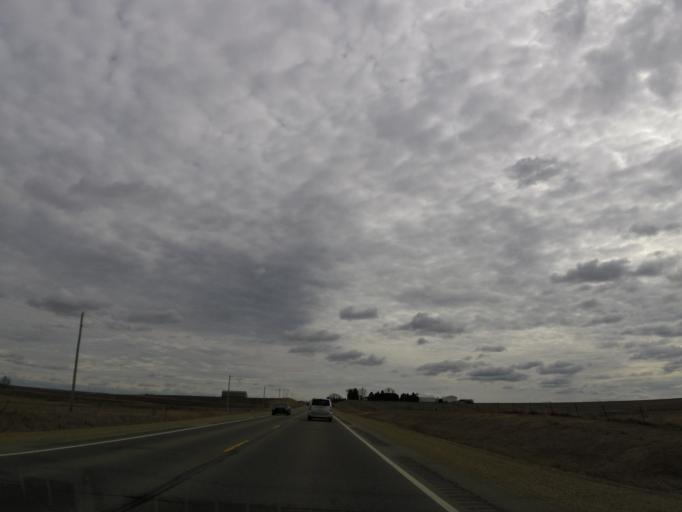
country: US
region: Iowa
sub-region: Chickasaw County
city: New Hampton
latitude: 43.1675
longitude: -92.2989
